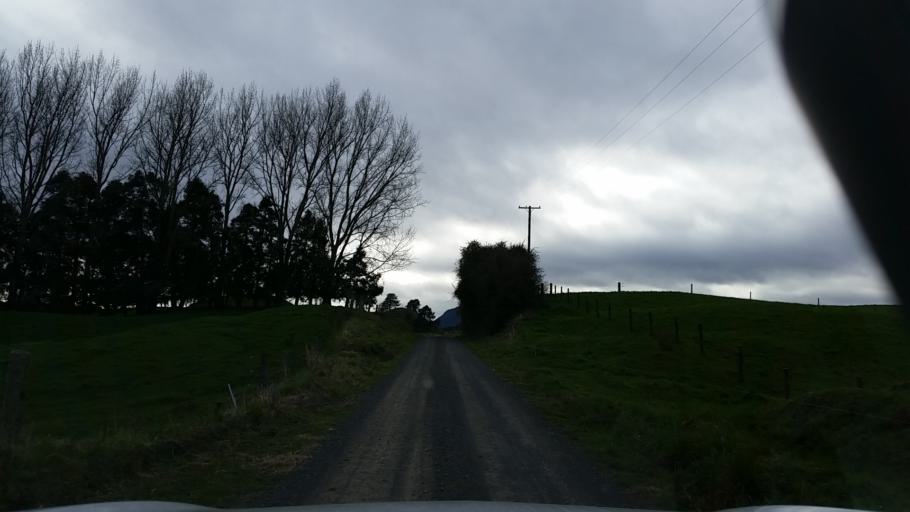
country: NZ
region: Bay of Plenty
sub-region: Rotorua District
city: Rotorua
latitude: -38.3057
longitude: 176.4165
